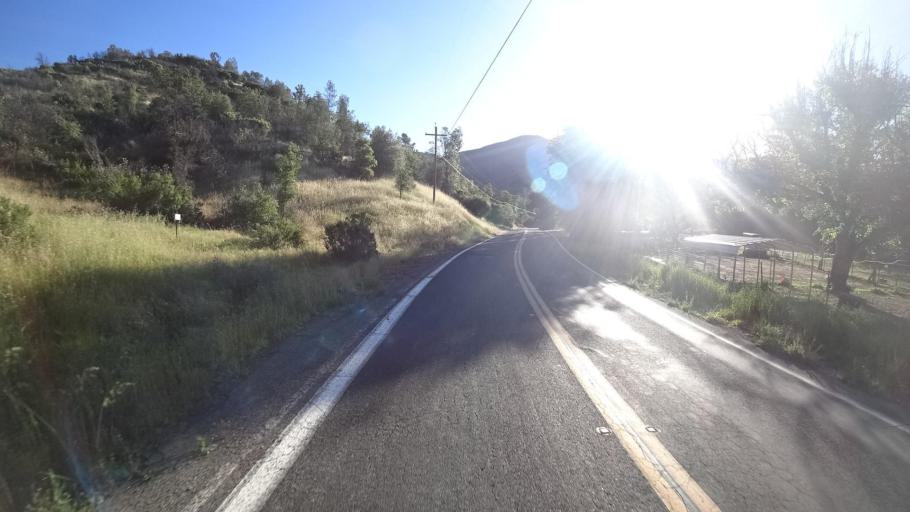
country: US
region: California
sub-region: Lake County
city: Upper Lake
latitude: 39.2096
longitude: -122.9187
